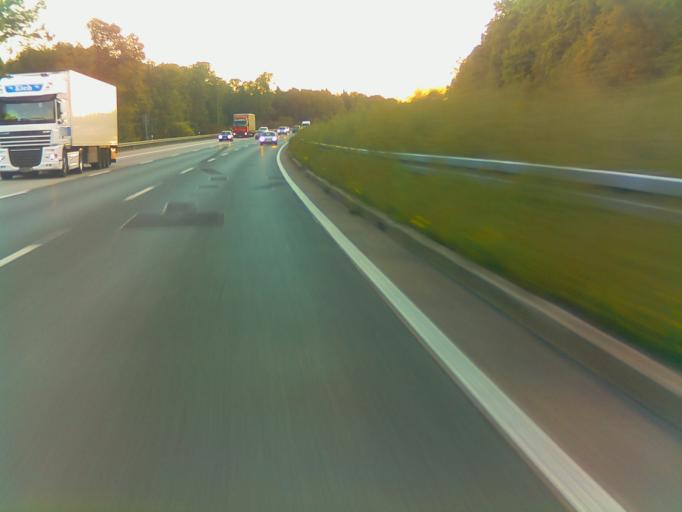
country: DE
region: Hesse
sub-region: Regierungsbezirk Darmstadt
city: Rosbach vor der Hohe
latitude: 50.3186
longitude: 8.6921
